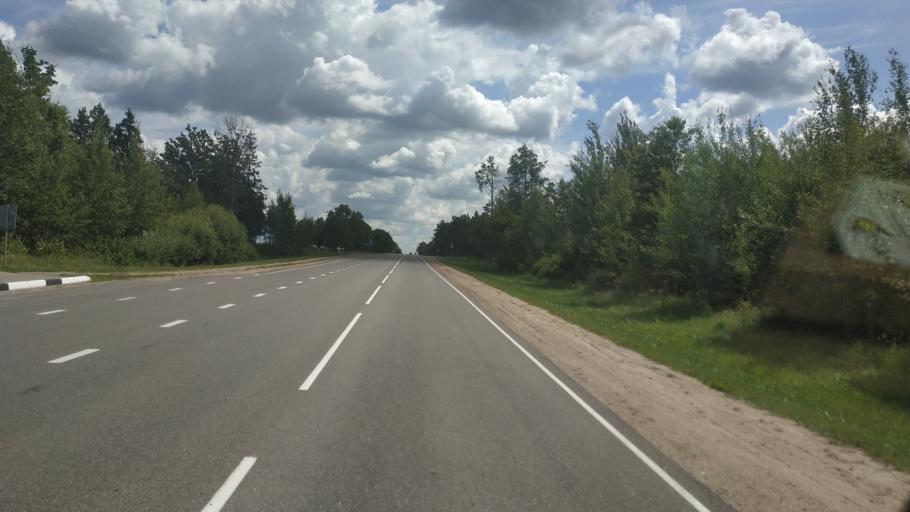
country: BY
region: Mogilev
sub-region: Mahilyowski Rayon
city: Veyno
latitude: 53.8214
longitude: 30.4324
